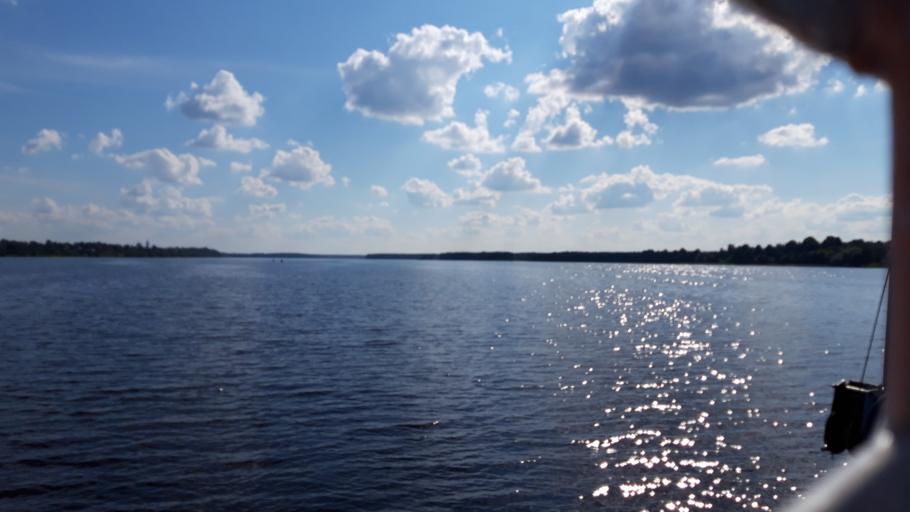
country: RU
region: Tverskaya
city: Zavidovo
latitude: 56.6503
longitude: 36.6258
